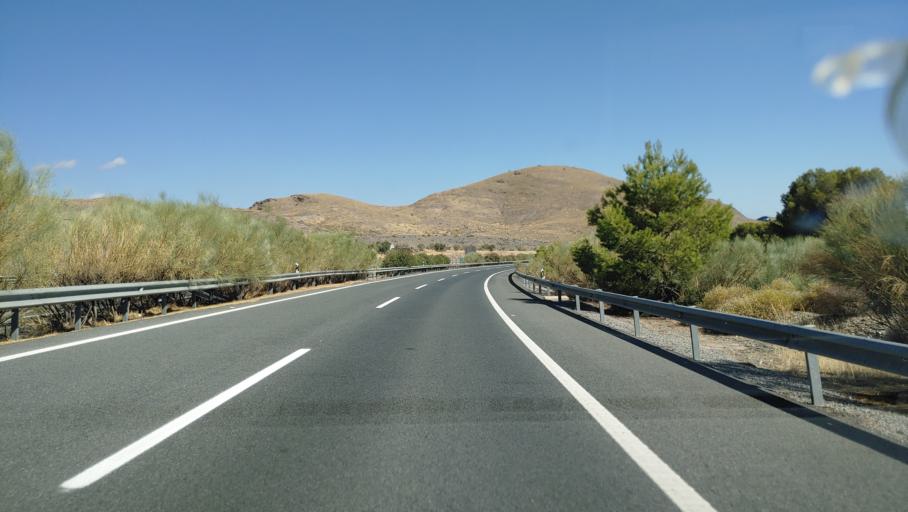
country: ES
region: Andalusia
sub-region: Provincia de Almeria
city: Gergal
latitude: 37.1362
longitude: -2.6459
